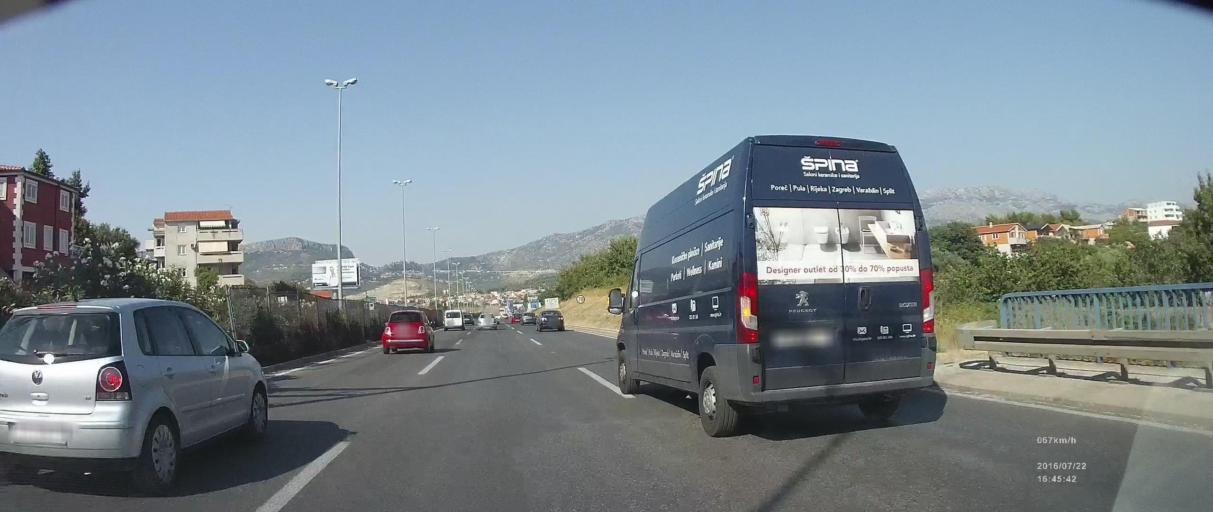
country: HR
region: Splitsko-Dalmatinska
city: Vranjic
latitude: 43.5210
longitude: 16.4837
